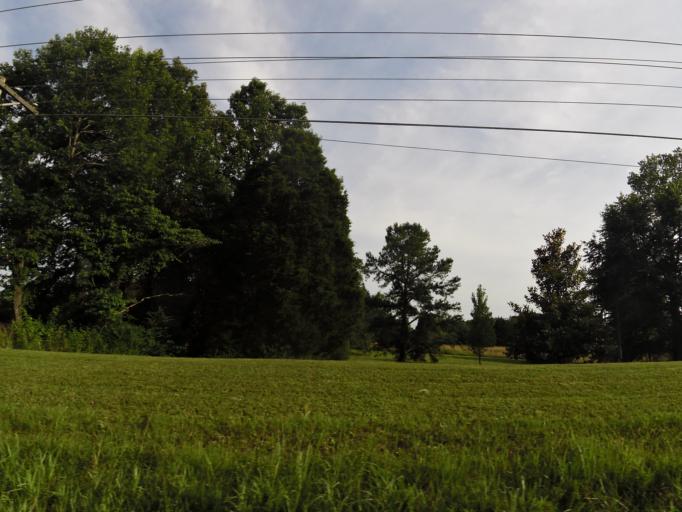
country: US
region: Tennessee
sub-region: Dickson County
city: Dickson
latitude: 36.0885
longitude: -87.4567
